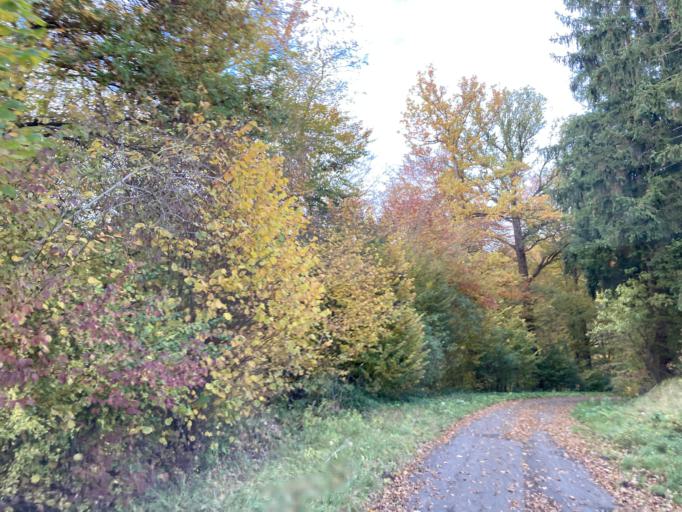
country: DE
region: Baden-Wuerttemberg
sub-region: Tuebingen Region
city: Dusslingen
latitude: 48.4804
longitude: 9.0664
